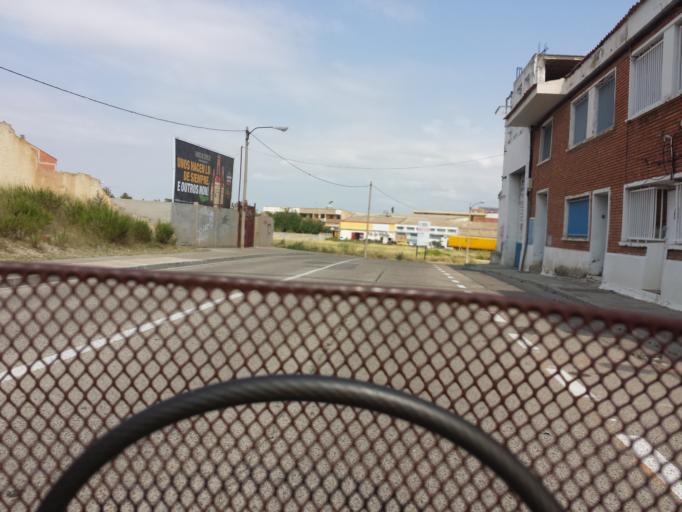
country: ES
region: Aragon
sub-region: Provincia de Zaragoza
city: Oliver-Valdefierro, Oliver, Valdefierro
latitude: 41.6416
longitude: -0.9253
